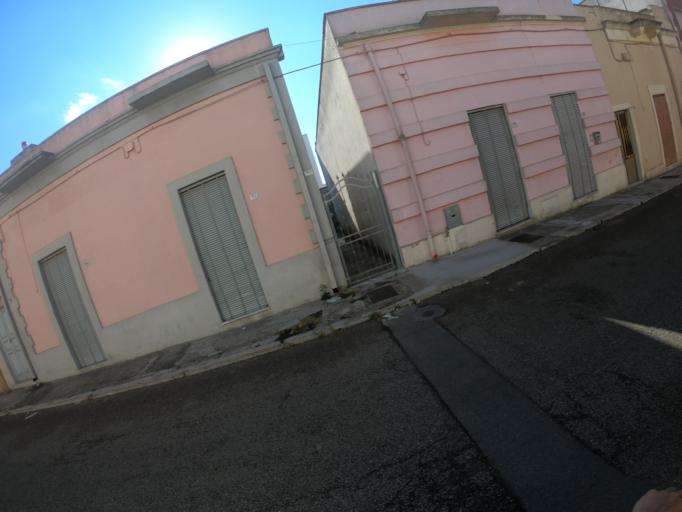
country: IT
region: Apulia
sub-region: Provincia di Lecce
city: Supersano
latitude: 40.0150
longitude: 18.2411
